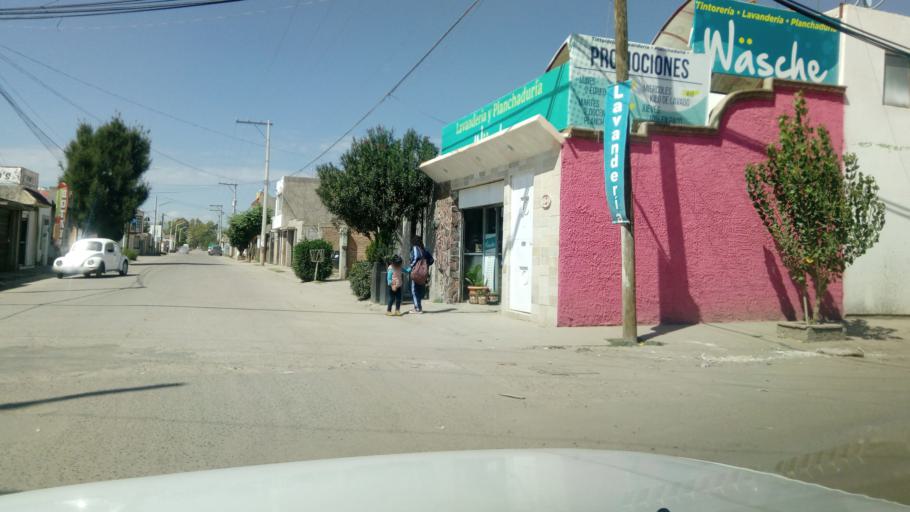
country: MX
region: Durango
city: Victoria de Durango
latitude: 23.9930
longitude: -104.6927
